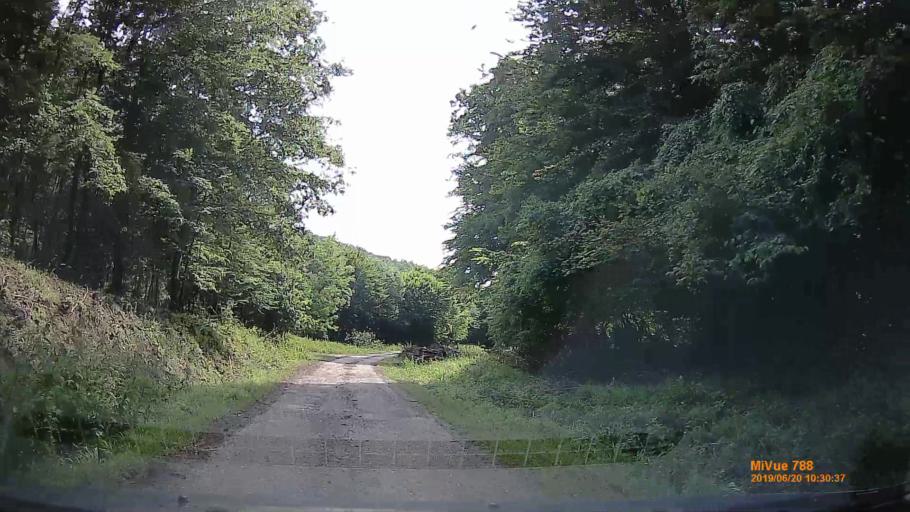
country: HU
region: Baranya
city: Mecseknadasd
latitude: 46.2071
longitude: 18.5015
